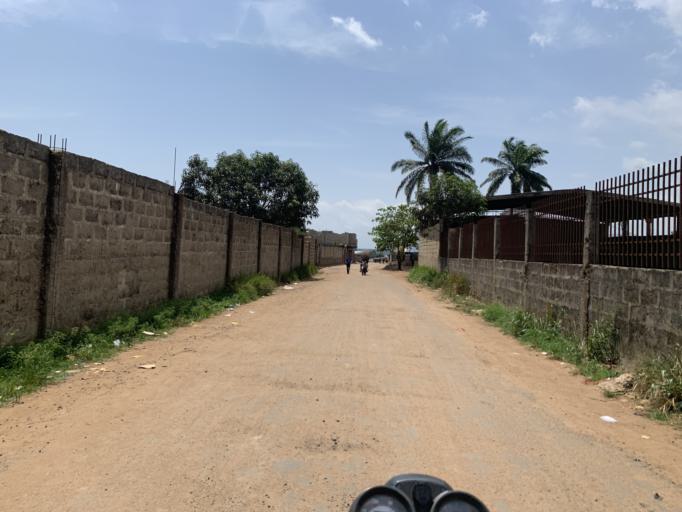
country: SL
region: Western Area
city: Waterloo
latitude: 8.3362
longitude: -13.0324
